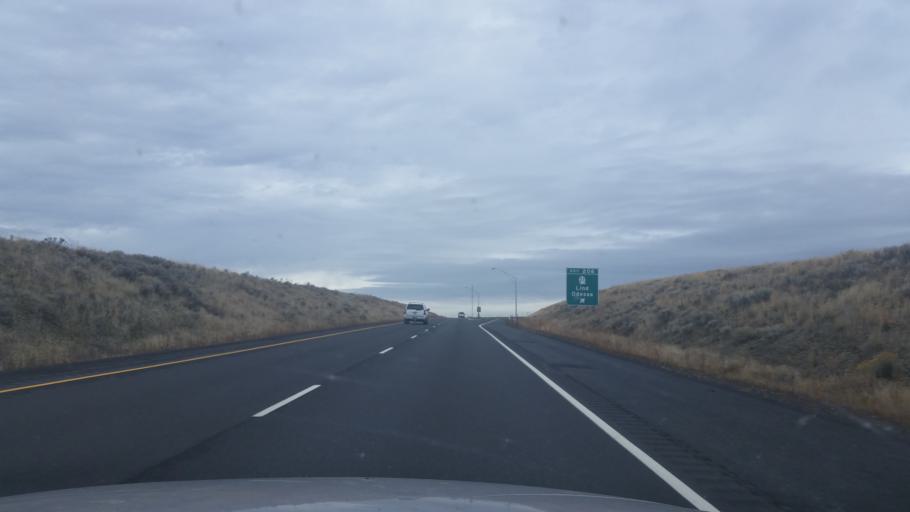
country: US
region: Washington
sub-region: Adams County
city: Ritzville
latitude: 47.0972
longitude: -118.6594
